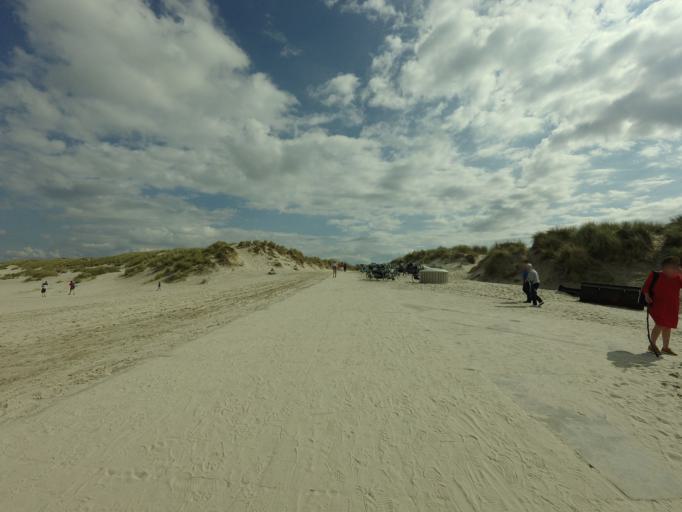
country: NL
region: Friesland
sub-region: Gemeente Terschelling
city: West-Terschelling
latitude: 53.4015
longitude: 5.2515
